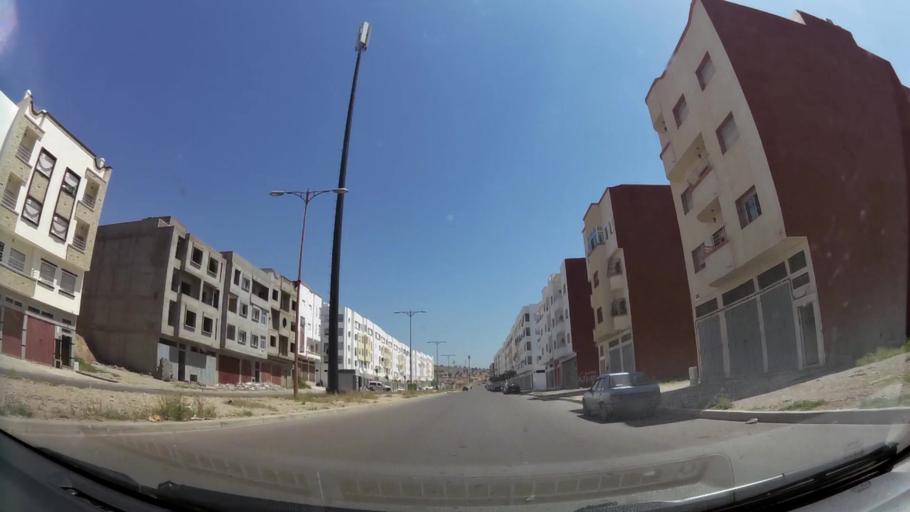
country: MA
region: Oued ed Dahab-Lagouira
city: Dakhla
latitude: 30.4355
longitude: -9.5534
